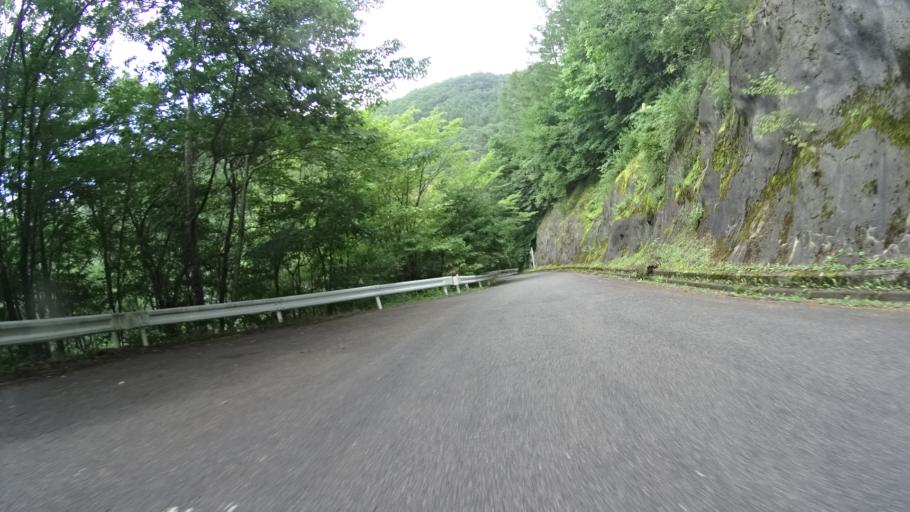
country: JP
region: Nagano
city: Saku
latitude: 36.0683
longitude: 138.6362
